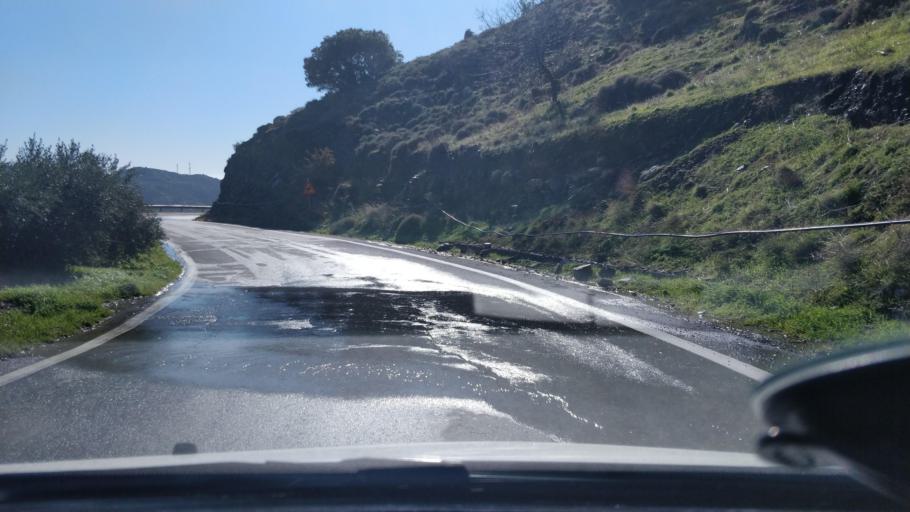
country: GR
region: Crete
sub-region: Nomos Irakleiou
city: Kastelli
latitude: 35.0386
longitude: 25.4445
